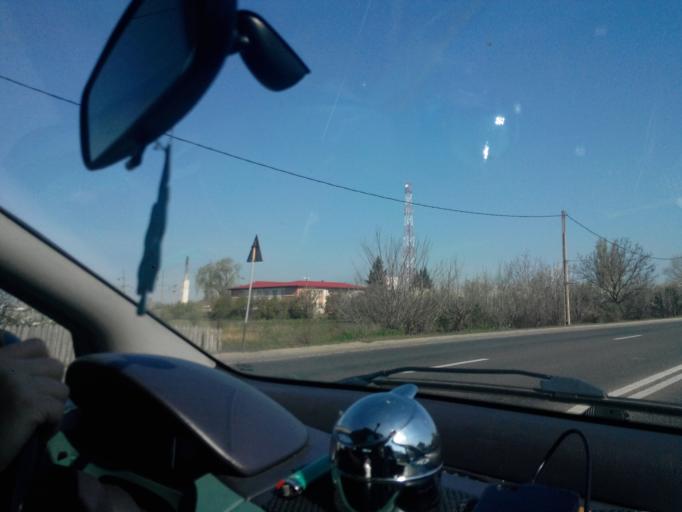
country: RO
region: Ilfov
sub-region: Comuna Ciolpani
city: Ciolpani
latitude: 44.6764
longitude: 26.0748
